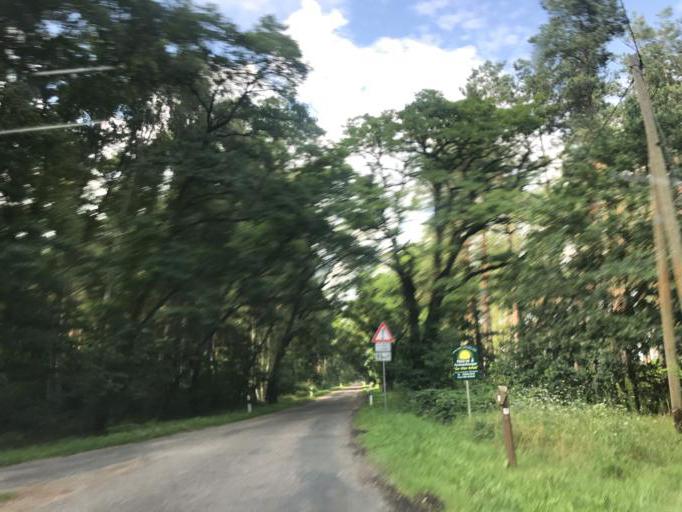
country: DE
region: Mecklenburg-Vorpommern
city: Wesenberg
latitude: 53.3208
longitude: 12.8620
